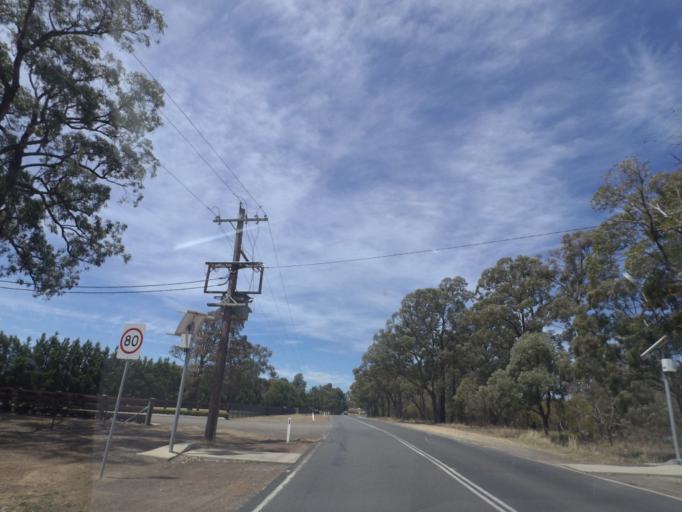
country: AU
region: New South Wales
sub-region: Wollondilly
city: Buxton
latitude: -34.3134
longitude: 150.5859
